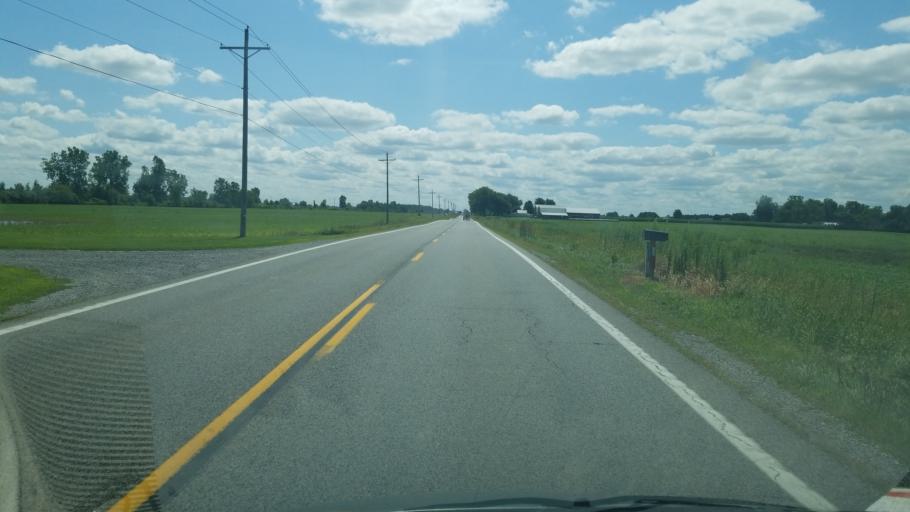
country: US
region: Ohio
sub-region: Fulton County
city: Delta
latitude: 41.6336
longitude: -84.0347
